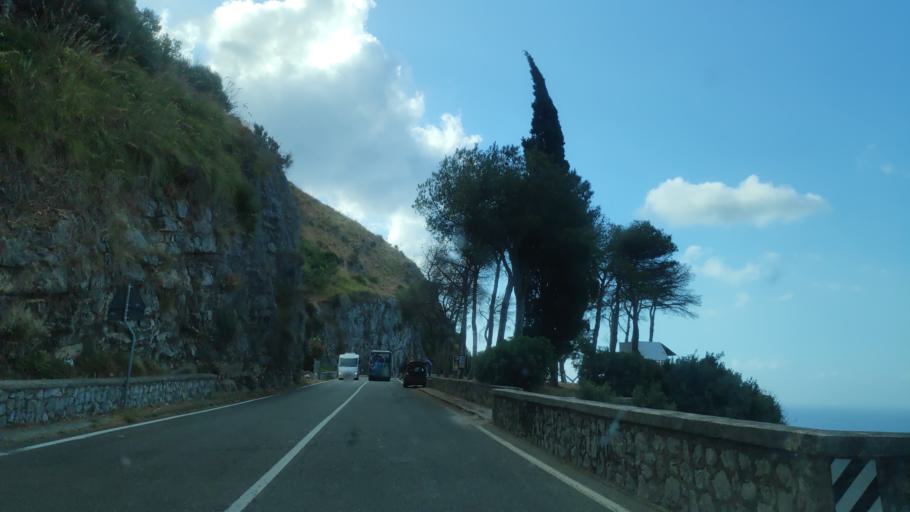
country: IT
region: Campania
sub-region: Provincia di Salerno
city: Positano
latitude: 40.6208
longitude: 14.4586
